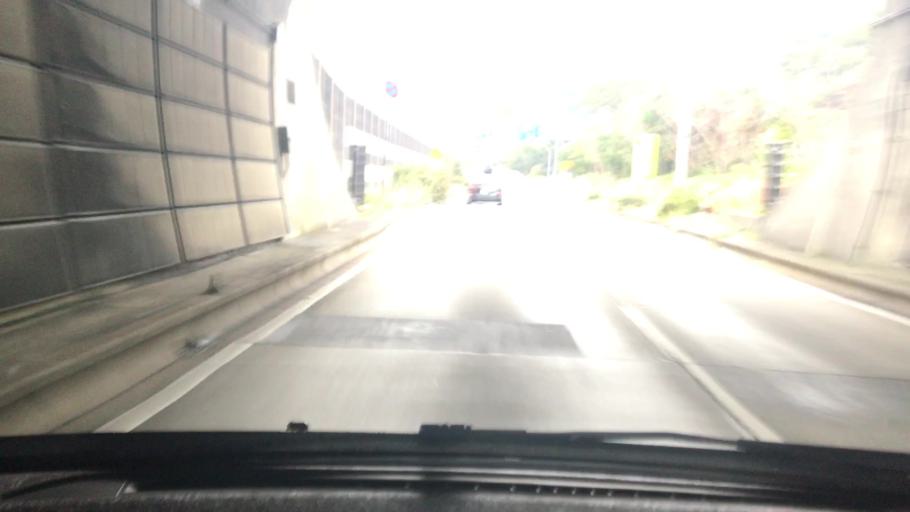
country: JP
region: Hyogo
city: Kobe
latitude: 34.7554
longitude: 135.1613
